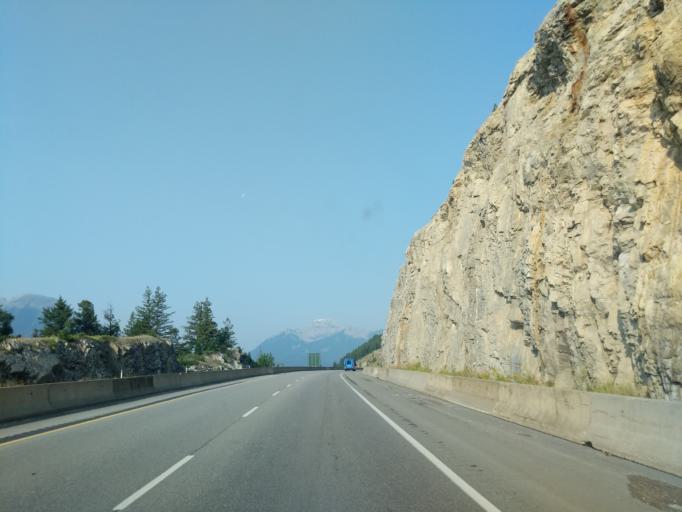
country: CA
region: Alberta
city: Banff
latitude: 51.1851
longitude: -115.5936
